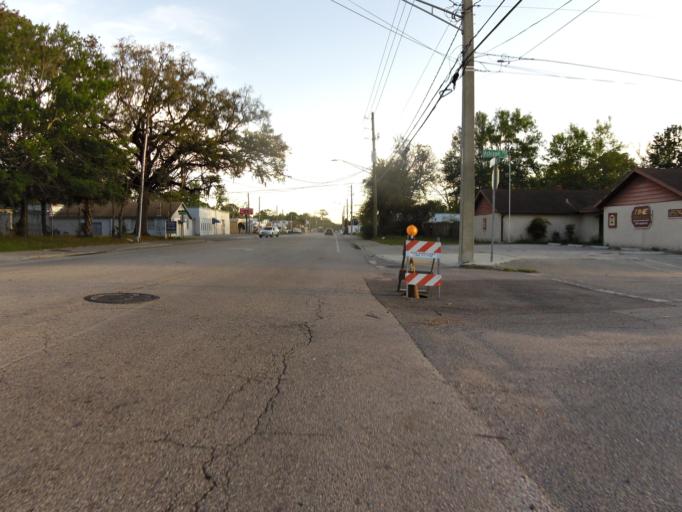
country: US
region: Florida
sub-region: Duval County
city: Jacksonville
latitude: 30.2893
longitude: -81.6441
